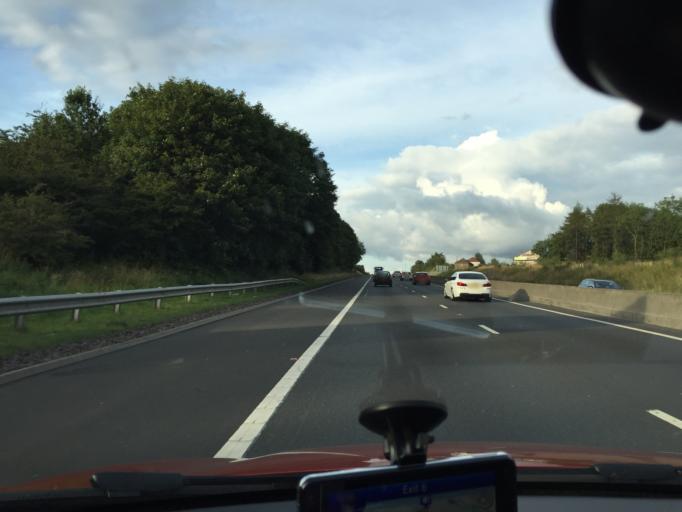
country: GB
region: Scotland
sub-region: North Lanarkshire
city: Cumbernauld
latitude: 55.9578
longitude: -3.9891
